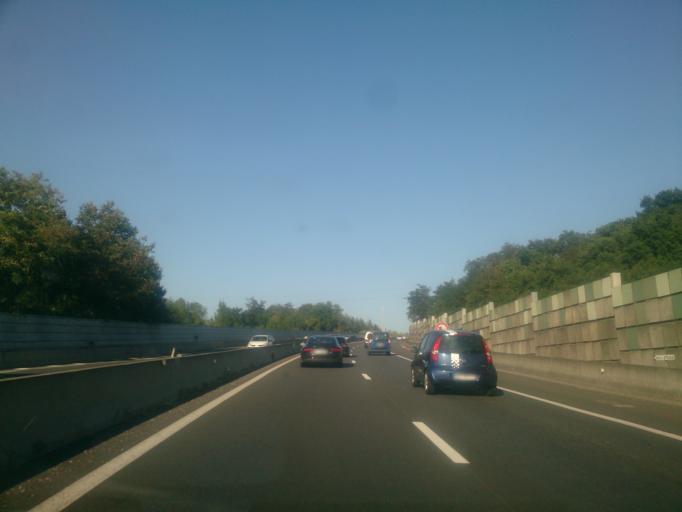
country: FR
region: Midi-Pyrenees
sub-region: Departement du Tarn-et-Garonne
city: Montauban
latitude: 43.9962
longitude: 1.3540
